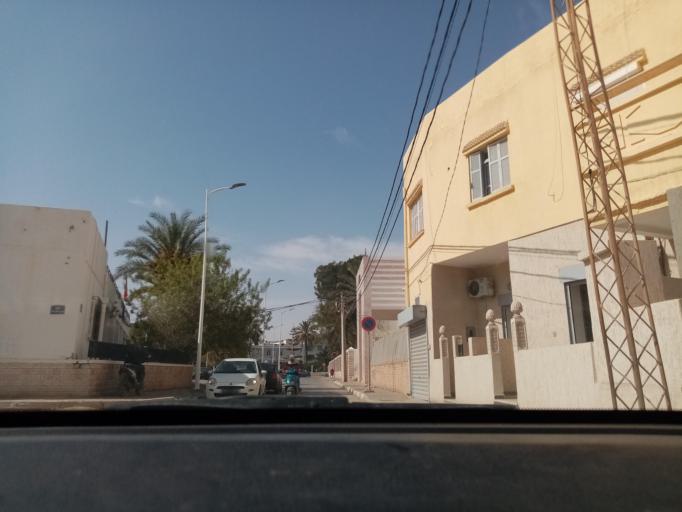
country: TN
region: Qabis
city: Gabes
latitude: 33.8868
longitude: 10.1016
